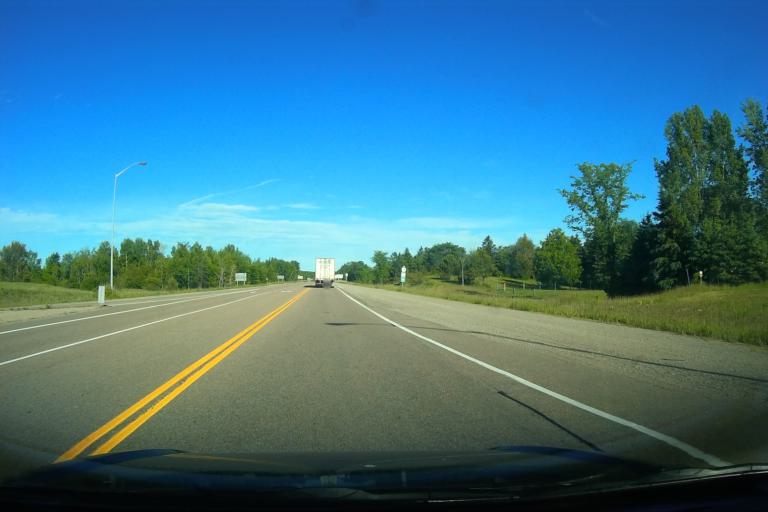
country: CA
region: Ontario
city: Renfrew
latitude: 45.5687
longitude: -76.7692
